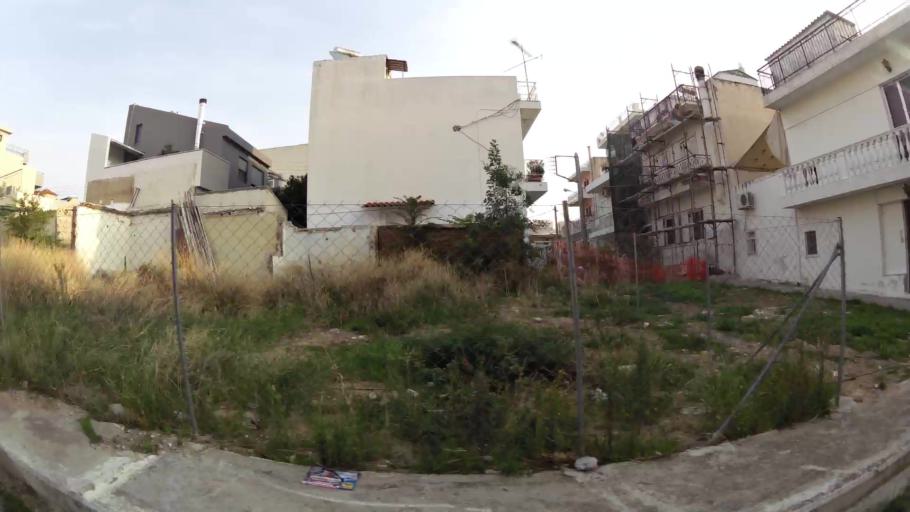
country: GR
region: Attica
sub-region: Nomarchia Athinas
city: Agios Dimitrios
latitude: 37.9372
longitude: 23.7261
